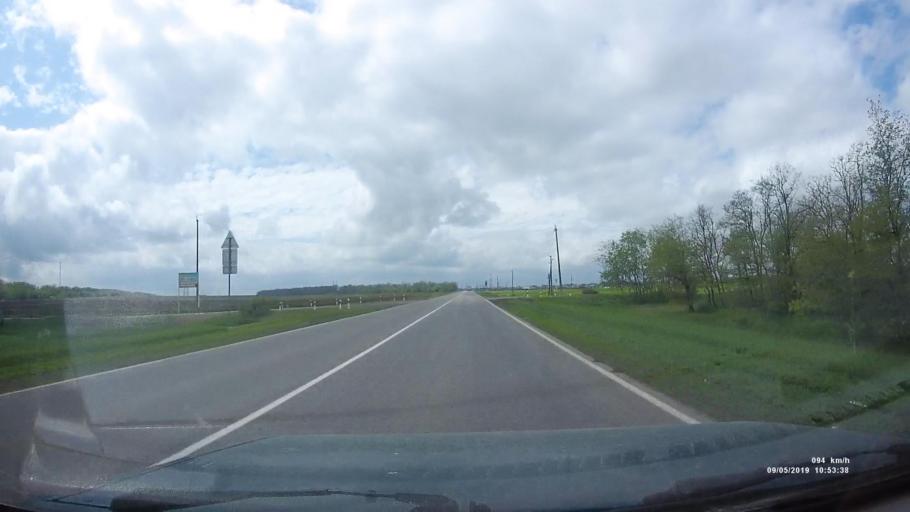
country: RU
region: Rostov
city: Peshkovo
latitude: 46.8863
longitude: 39.3382
